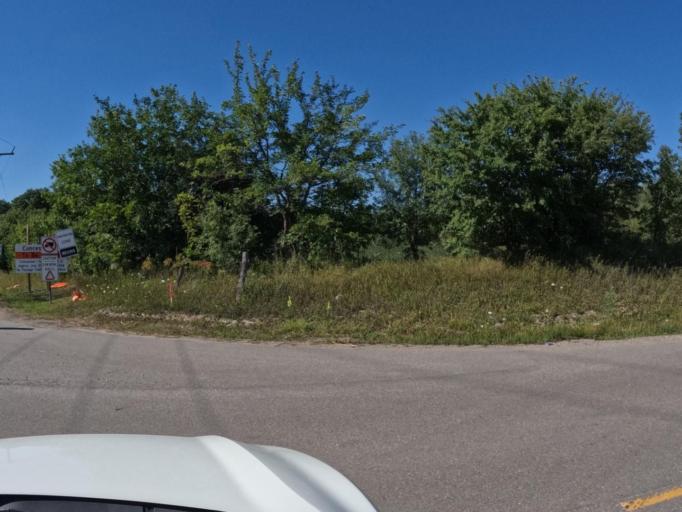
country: CA
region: Ontario
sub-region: Wellington County
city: Guelph
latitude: 43.4280
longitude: -80.1266
